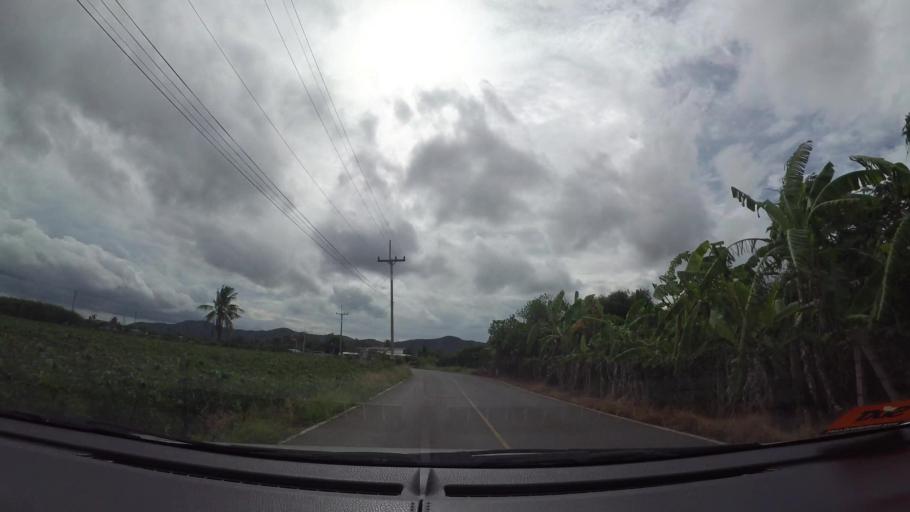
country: TH
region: Chon Buri
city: Sattahip
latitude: 12.7205
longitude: 100.9077
